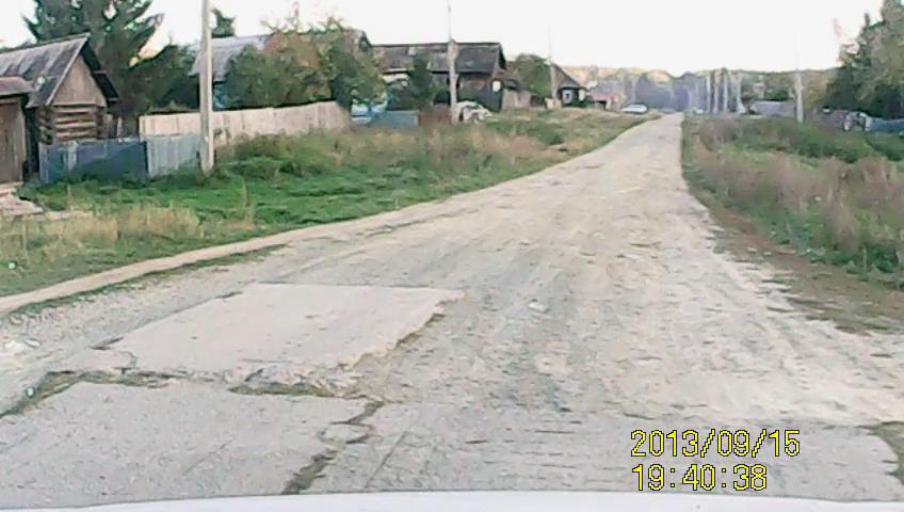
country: RU
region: Chelyabinsk
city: Kyshtym
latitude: 55.8477
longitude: 60.4817
